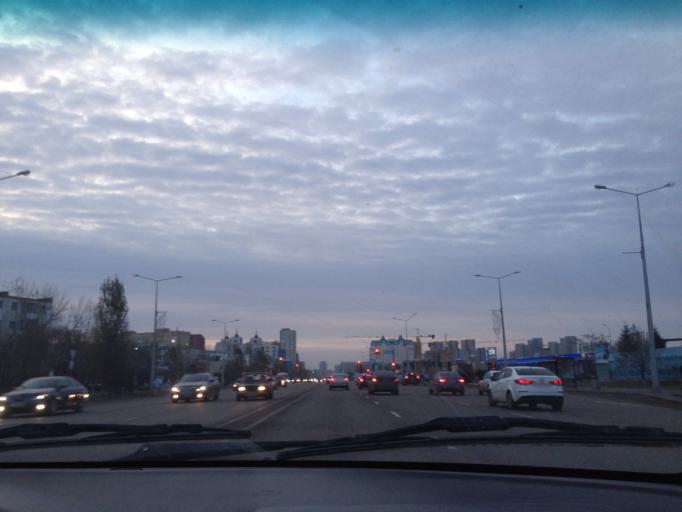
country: KZ
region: Astana Qalasy
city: Astana
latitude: 51.1473
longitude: 71.4590
